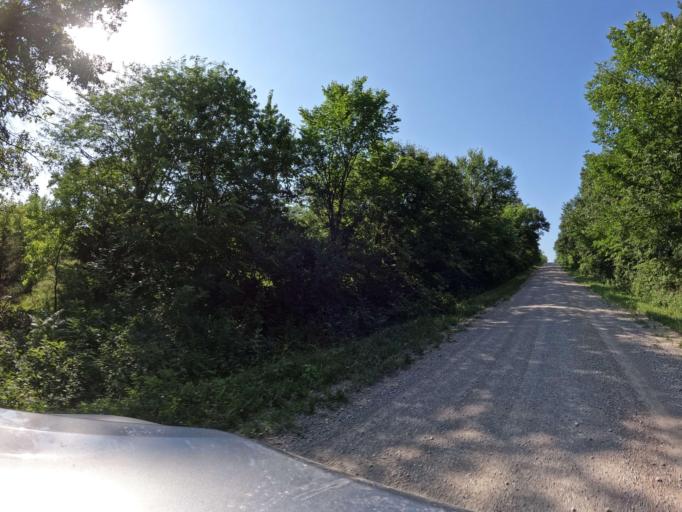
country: US
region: Iowa
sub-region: Appanoose County
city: Centerville
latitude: 40.7336
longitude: -93.0207
